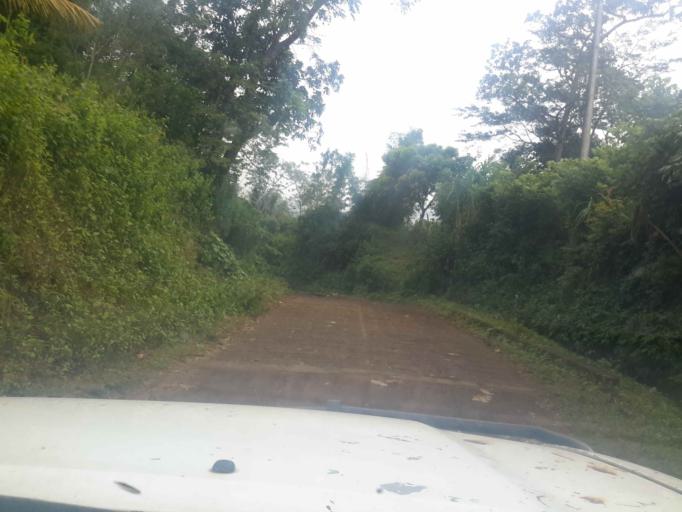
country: NI
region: Carazo
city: San Marcos
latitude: 11.8861
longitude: -86.1840
